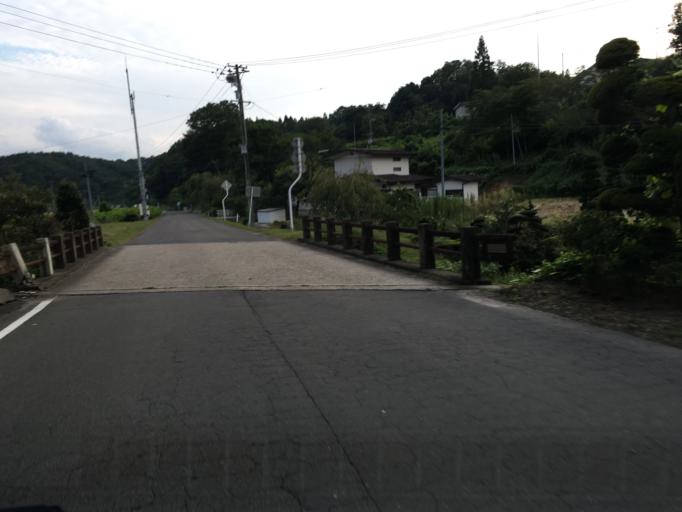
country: JP
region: Fukushima
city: Fukushima-shi
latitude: 37.6949
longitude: 140.5590
